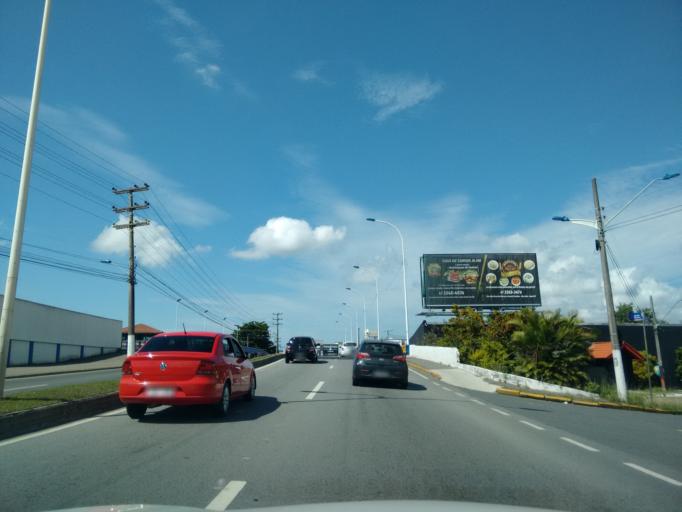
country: BR
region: Santa Catarina
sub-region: Itajai
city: Itajai
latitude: -26.8892
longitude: -48.6846
